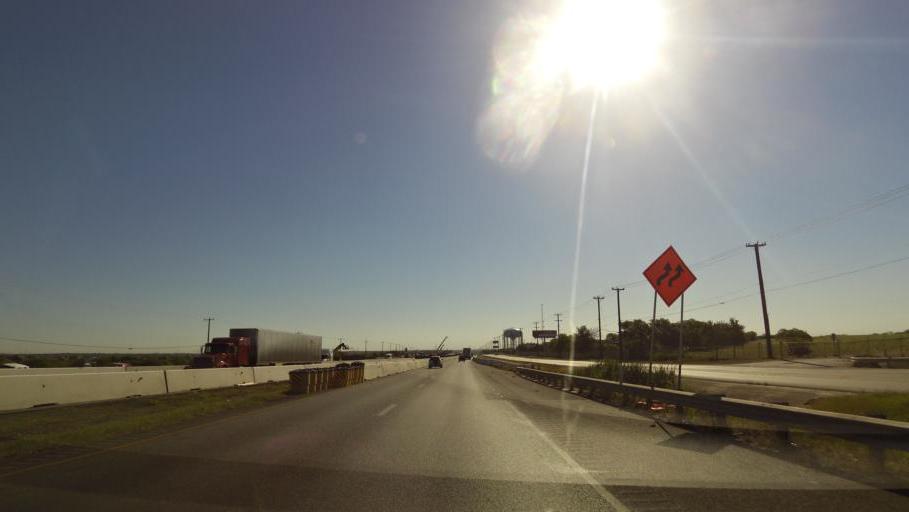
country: US
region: Texas
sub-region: Bexar County
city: Kirby
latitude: 29.4479
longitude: -98.3510
